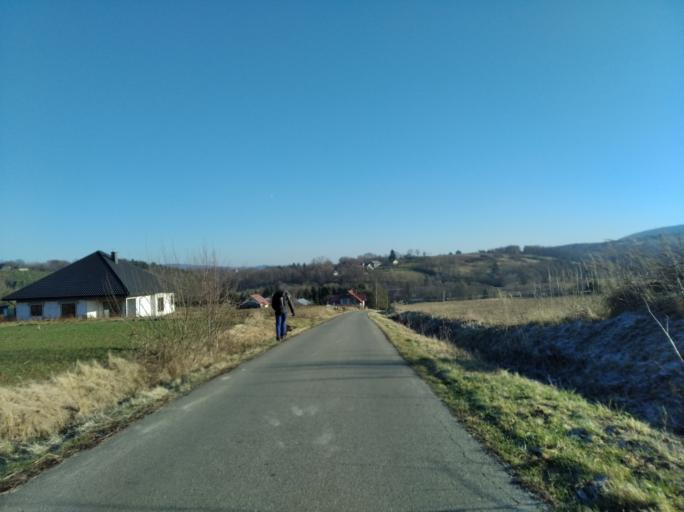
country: PL
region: Subcarpathian Voivodeship
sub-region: Powiat strzyzowski
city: Wysoka Strzyzowska
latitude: 49.8513
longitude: 21.7554
